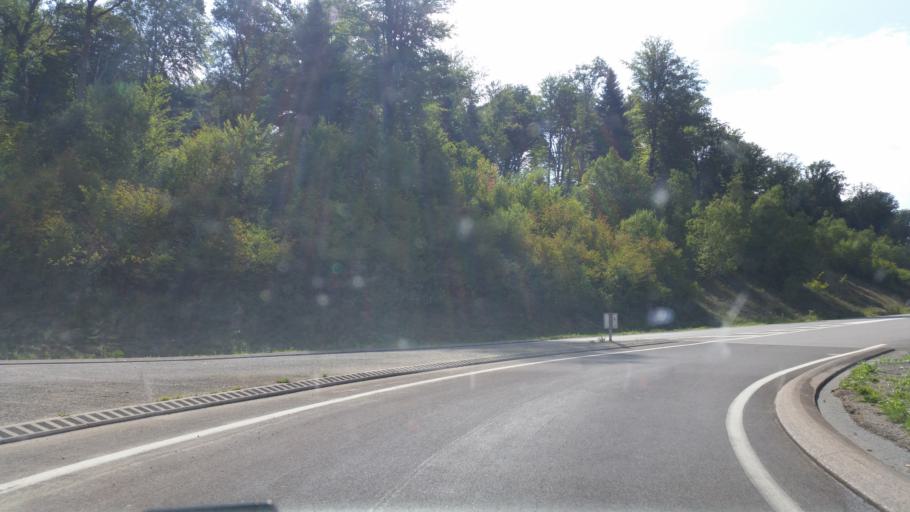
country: FR
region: Franche-Comte
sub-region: Departement du Doubs
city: Voujeaucourt
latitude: 47.4593
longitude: 6.7611
